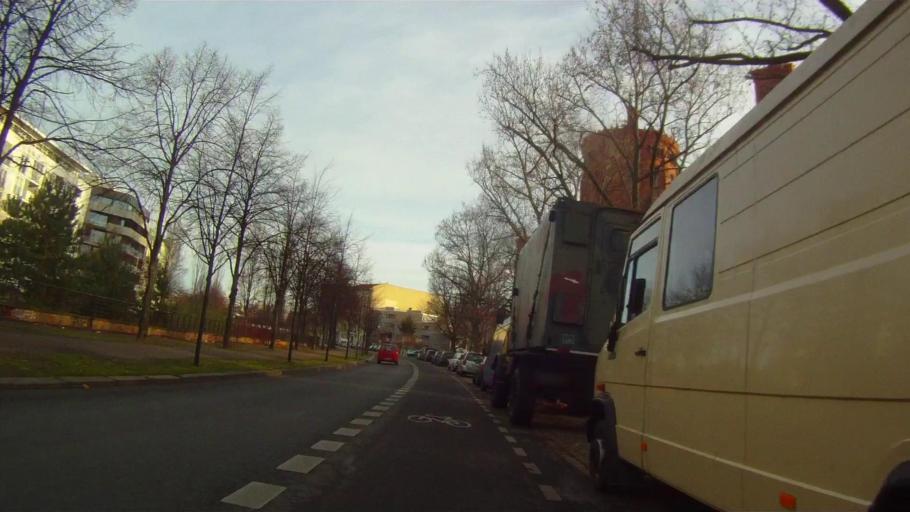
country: DE
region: Berlin
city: Bezirk Kreuzberg
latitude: 52.5053
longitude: 13.4250
